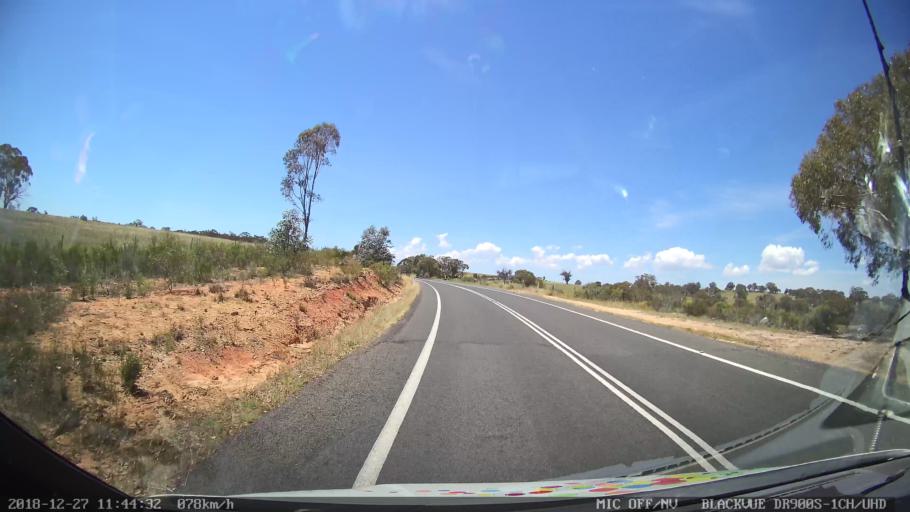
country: AU
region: New South Wales
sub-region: Bathurst Regional
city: Perthville
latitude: -33.5733
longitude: 149.4756
